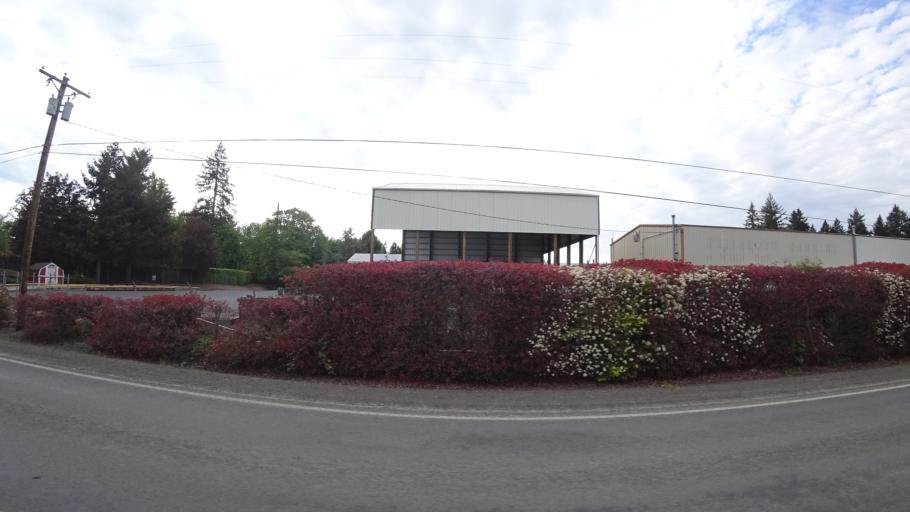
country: US
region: Oregon
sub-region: Washington County
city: Hillsboro
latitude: 45.4824
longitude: -122.9838
